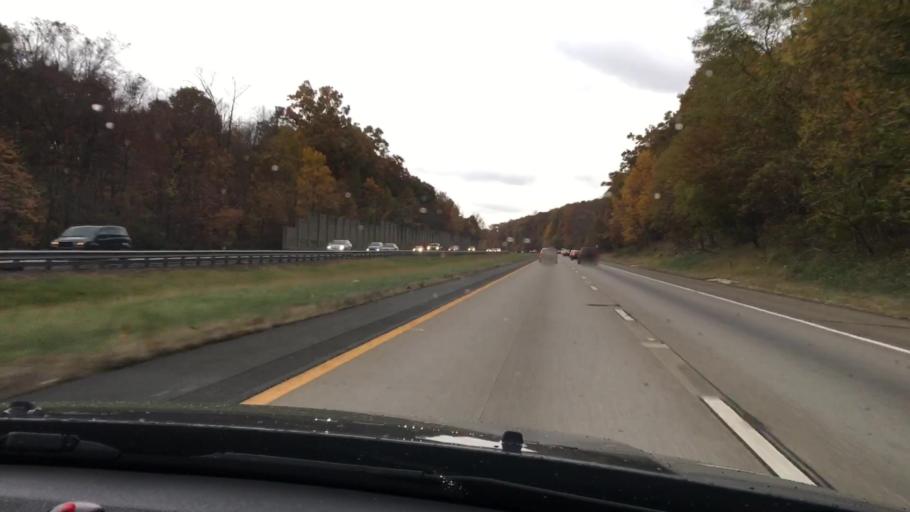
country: US
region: New Jersey
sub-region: Bergen County
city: Franklin Lakes
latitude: 41.0483
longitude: -74.1903
